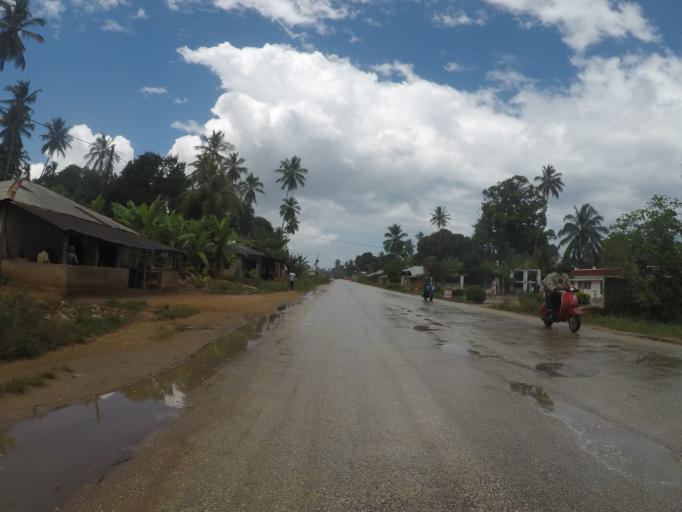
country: TZ
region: Zanzibar Central/South
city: Koani
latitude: -6.0448
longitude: 39.2277
